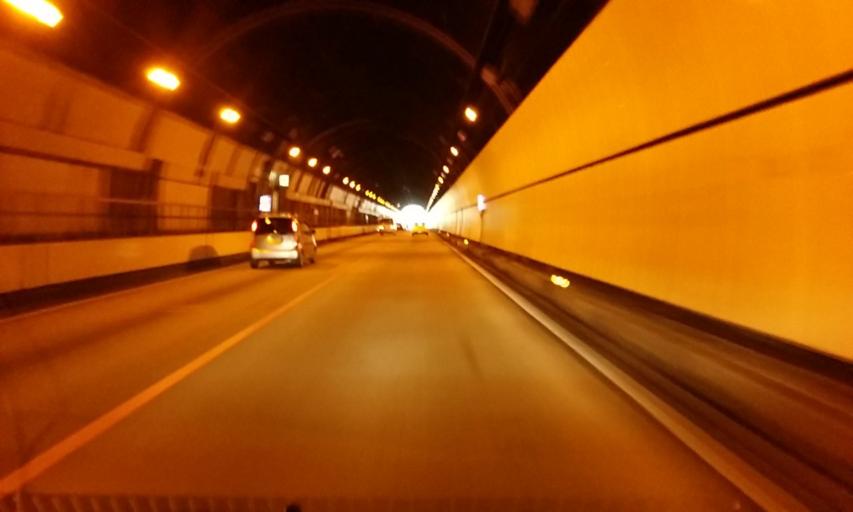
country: JP
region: Hyogo
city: Sasayama
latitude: 35.1185
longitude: 135.1649
